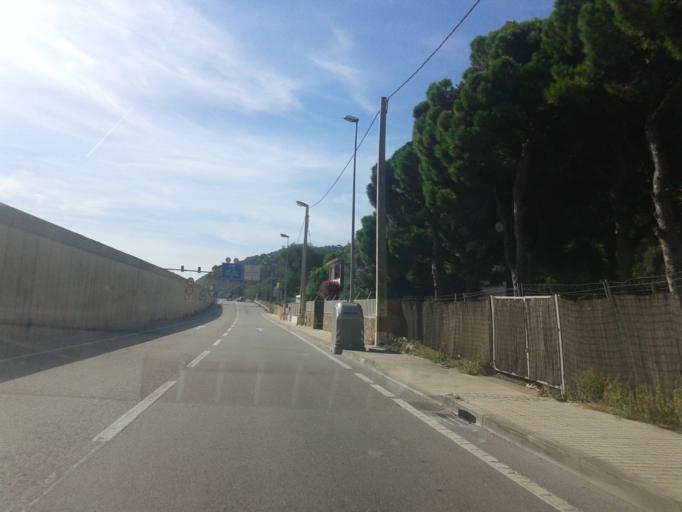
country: ES
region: Catalonia
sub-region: Provincia de Barcelona
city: Castelldefels
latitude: 41.2647
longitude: 1.9344
